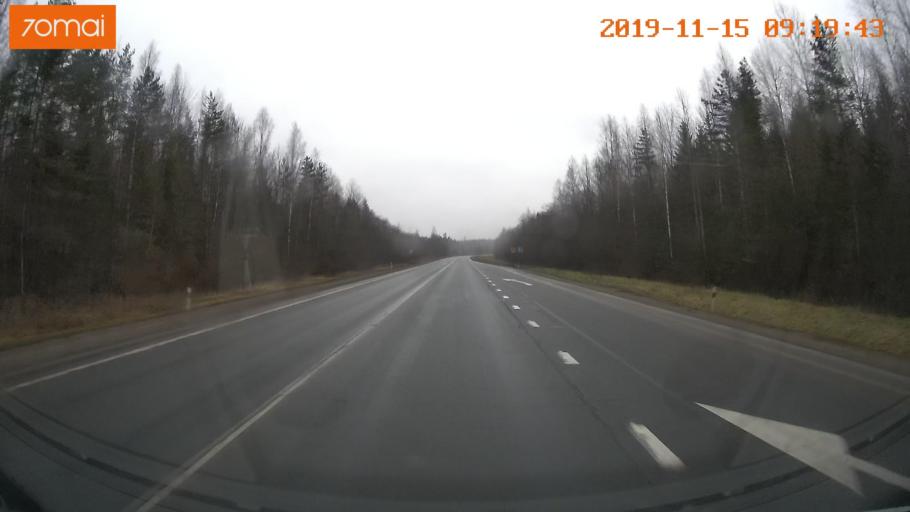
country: RU
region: Vologda
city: Tonshalovo
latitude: 59.2860
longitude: 38.0212
